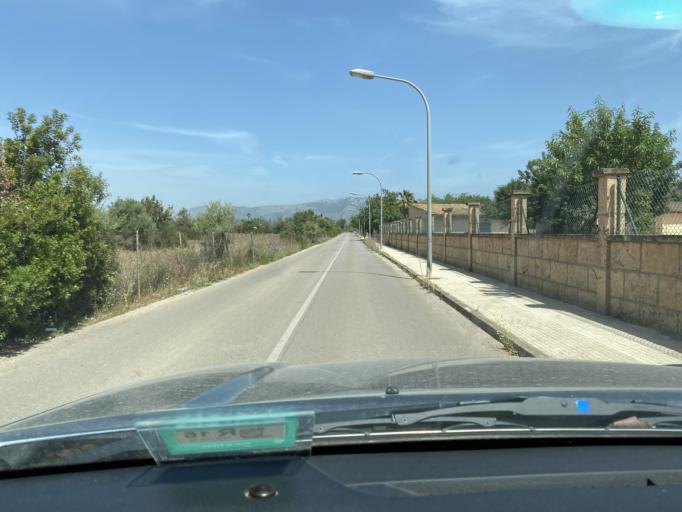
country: ES
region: Balearic Islands
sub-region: Illes Balears
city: Marratxi
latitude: 39.6302
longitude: 2.7104
